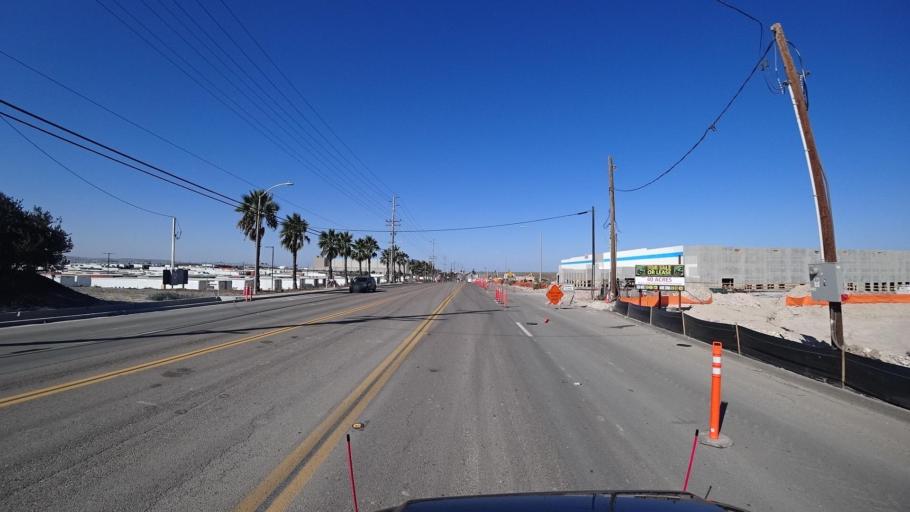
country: MX
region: Baja California
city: Tijuana
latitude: 32.5674
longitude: -116.9231
